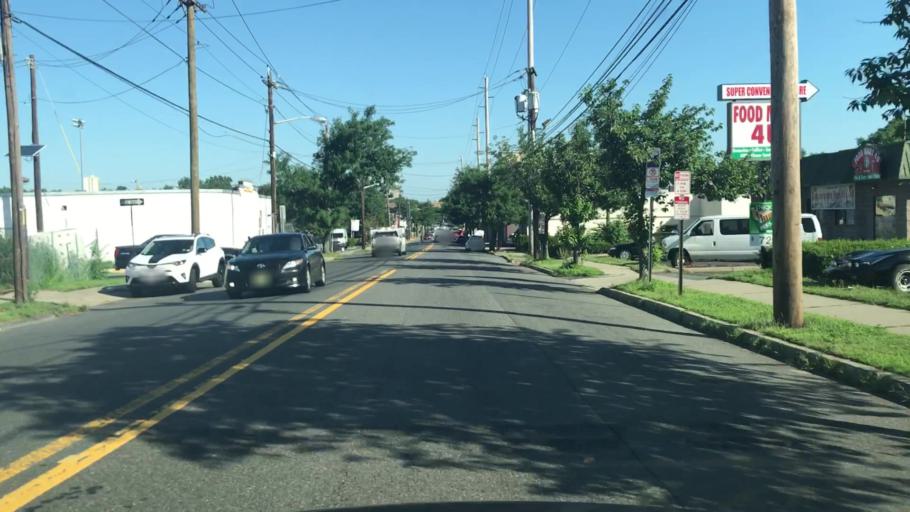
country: US
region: New Jersey
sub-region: Bergen County
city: Wallington
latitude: 40.8473
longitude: -74.1118
